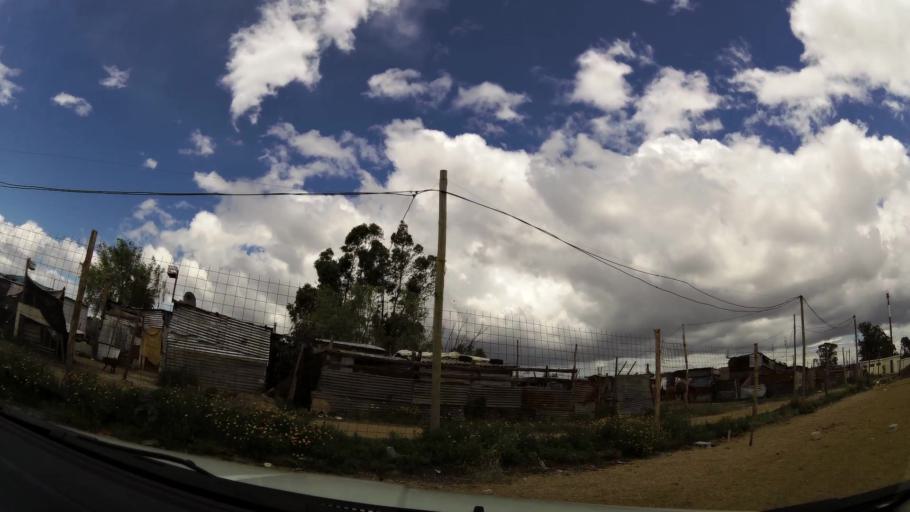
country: UY
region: Montevideo
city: Montevideo
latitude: -34.8223
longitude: -56.1640
